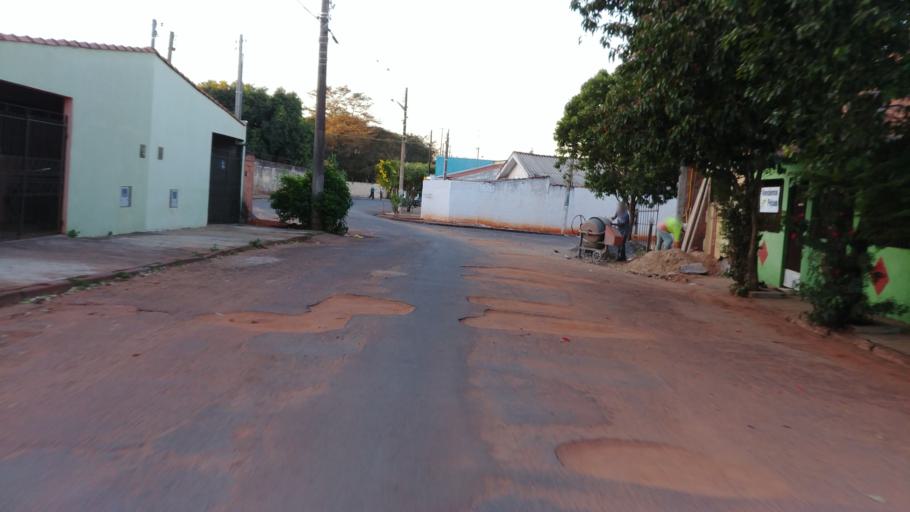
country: BR
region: Sao Paulo
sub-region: Paraguacu Paulista
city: Paraguacu Paulista
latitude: -22.4283
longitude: -50.5757
